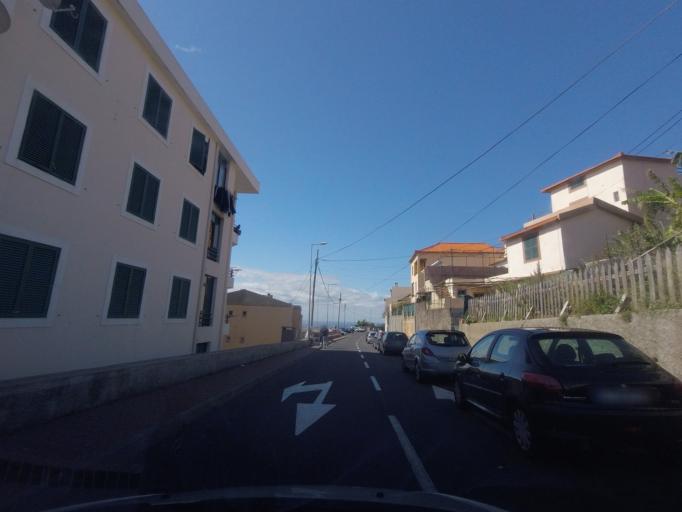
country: PT
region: Madeira
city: Camara de Lobos
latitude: 32.6529
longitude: -16.9716
